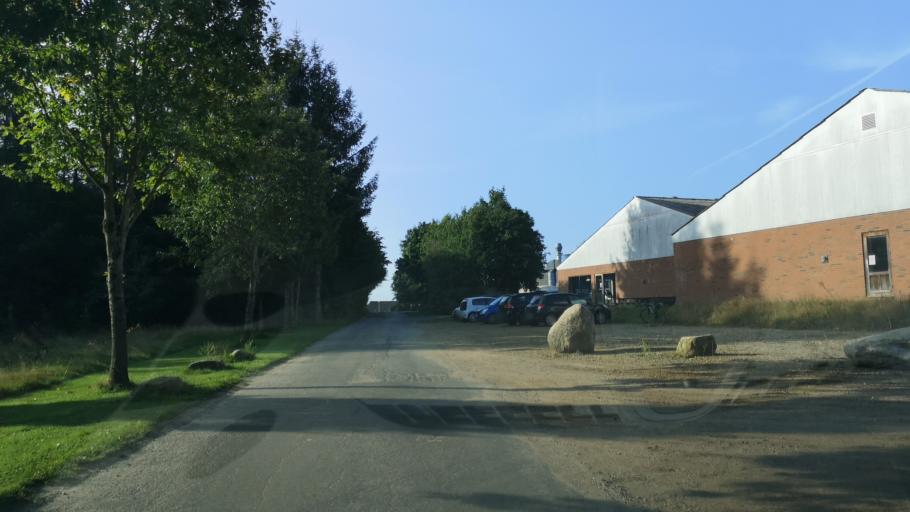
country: DK
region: Central Jutland
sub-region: Herning Kommune
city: Snejbjerg
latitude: 56.1364
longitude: 8.9183
